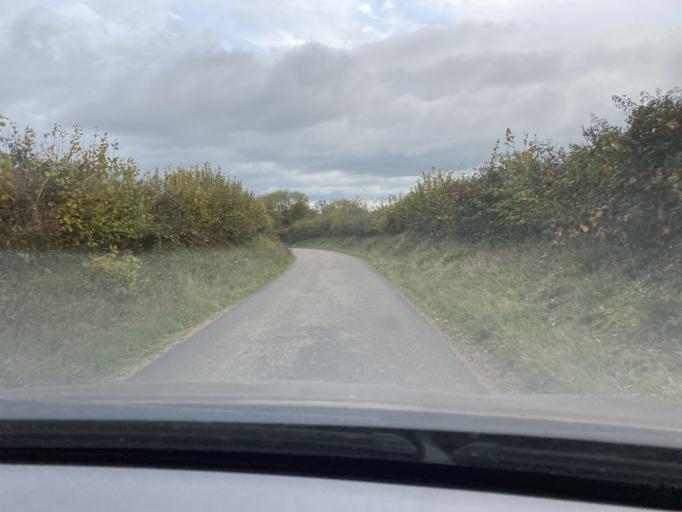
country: FR
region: Bourgogne
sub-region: Departement de la Cote-d'Or
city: Saulieu
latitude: 47.2863
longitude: 4.2210
